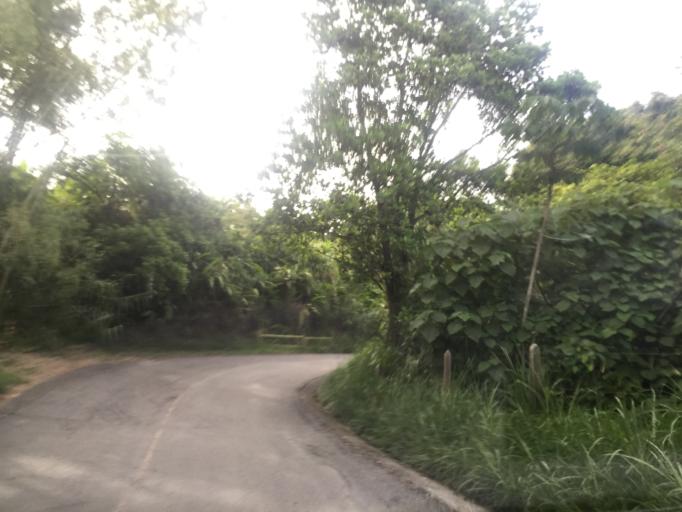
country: CO
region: Quindio
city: La Tebaida
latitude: 4.4653
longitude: -75.8110
